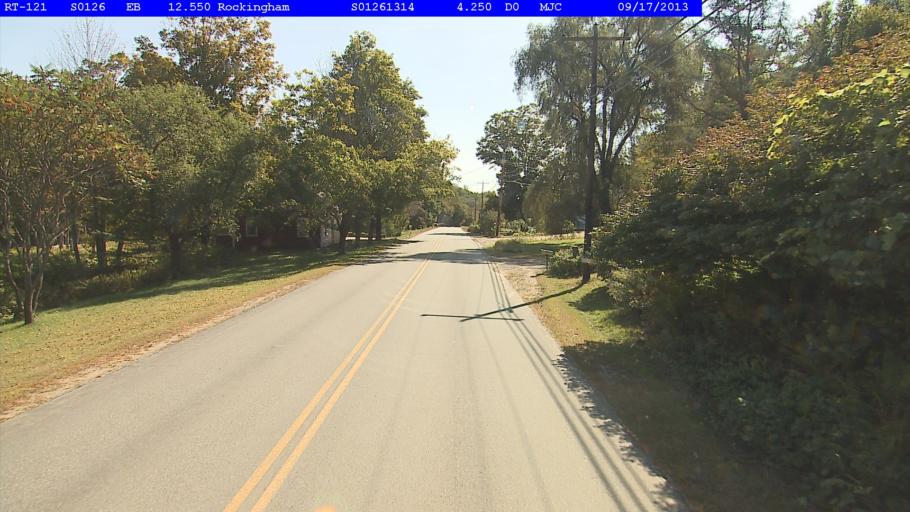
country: US
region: Vermont
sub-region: Windham County
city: Bellows Falls
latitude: 43.1369
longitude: -72.4872
